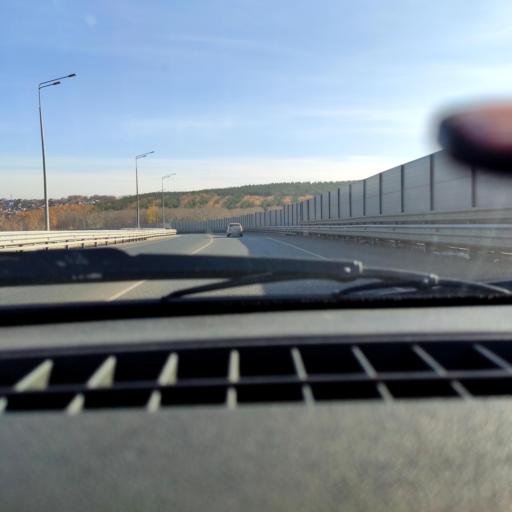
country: RU
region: Bashkortostan
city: Ufa
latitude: 54.8266
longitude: 56.1259
